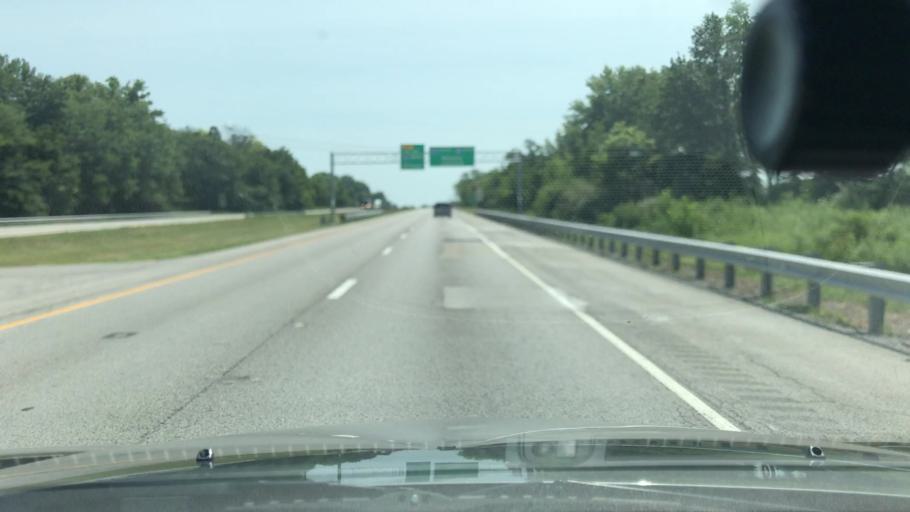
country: US
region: Illinois
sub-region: Jefferson County
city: Mount Vernon
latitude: 38.3417
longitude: -88.9679
